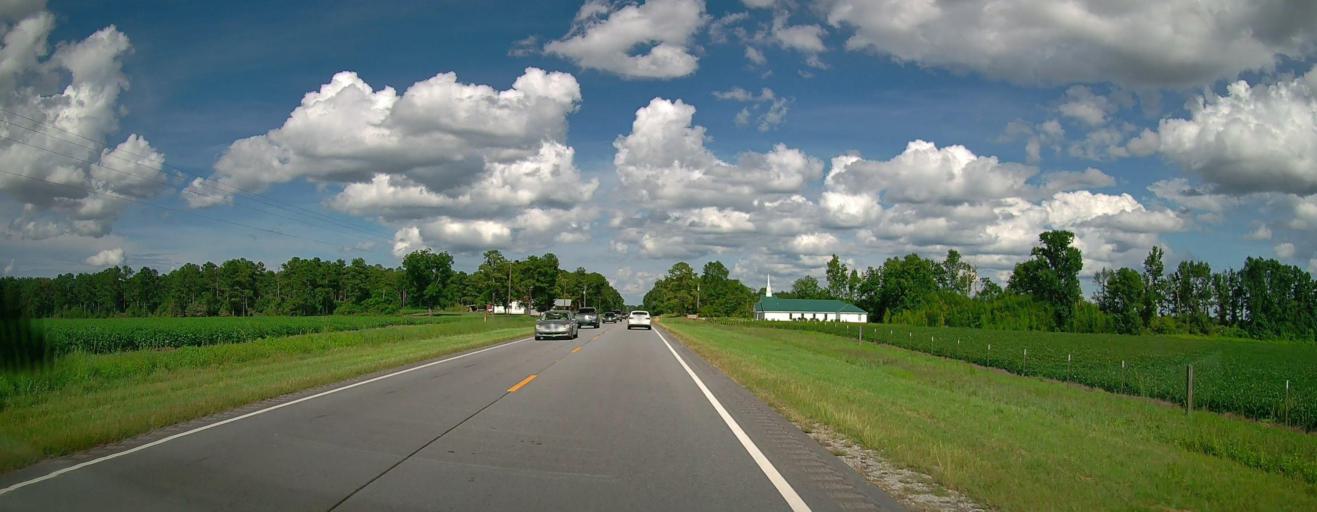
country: US
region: Alabama
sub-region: Lee County
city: Auburn
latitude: 32.4366
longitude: -85.3949
